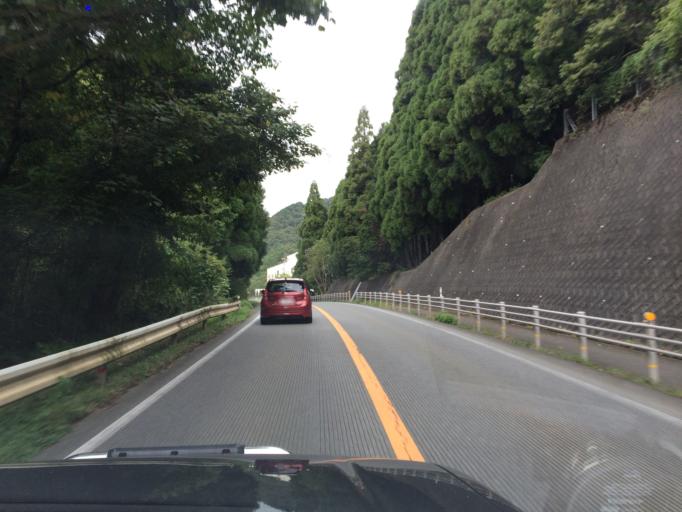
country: JP
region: Hyogo
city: Toyooka
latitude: 35.3644
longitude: 134.8255
